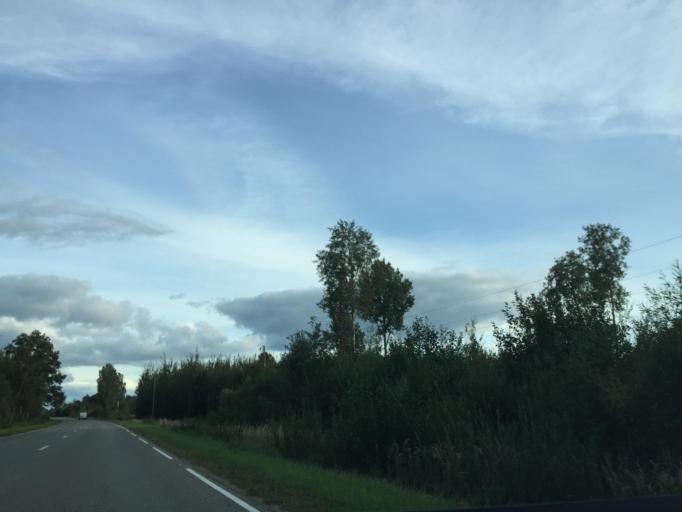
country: LV
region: Nereta
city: Nereta
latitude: 56.3372
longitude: 25.0677
